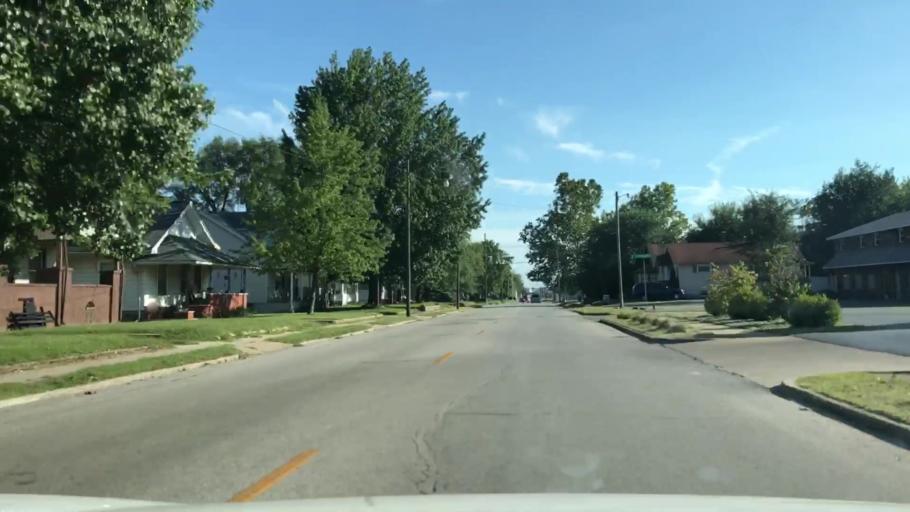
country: US
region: Illinois
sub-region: Madison County
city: Wood River
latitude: 38.8674
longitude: -90.0986
